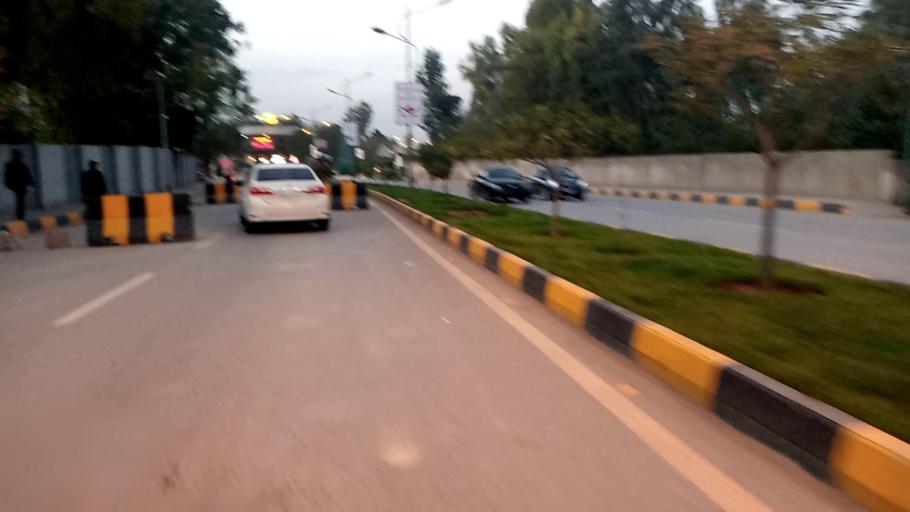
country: PK
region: Khyber Pakhtunkhwa
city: Peshawar
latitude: 34.0166
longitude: 71.5482
